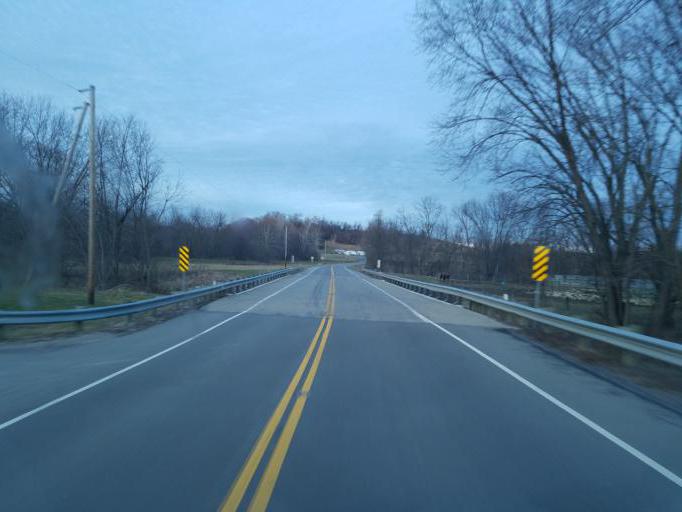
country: US
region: Ohio
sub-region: Muskingum County
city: Dresden
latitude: 40.1640
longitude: -82.0256
